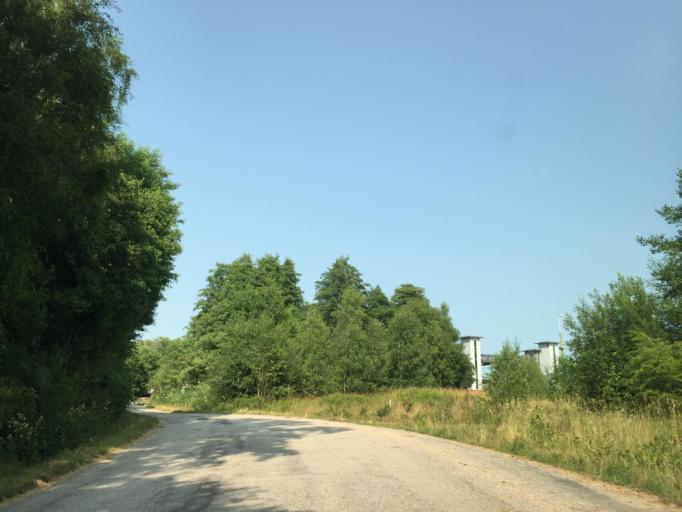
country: SE
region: Vaestra Goetaland
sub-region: Vanersborgs Kommun
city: Vanersborg
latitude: 58.3586
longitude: 12.2722
